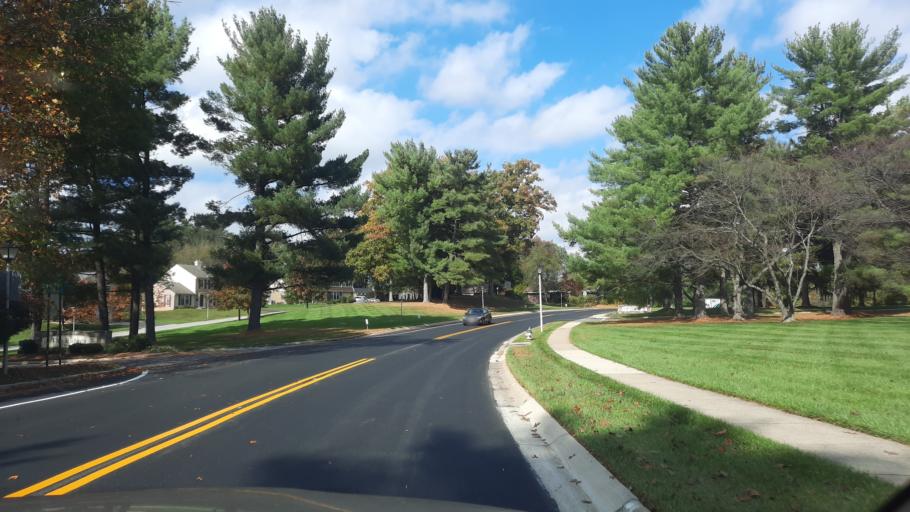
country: US
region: Maryland
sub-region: Montgomery County
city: Montgomery Village
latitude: 39.1721
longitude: -77.2167
